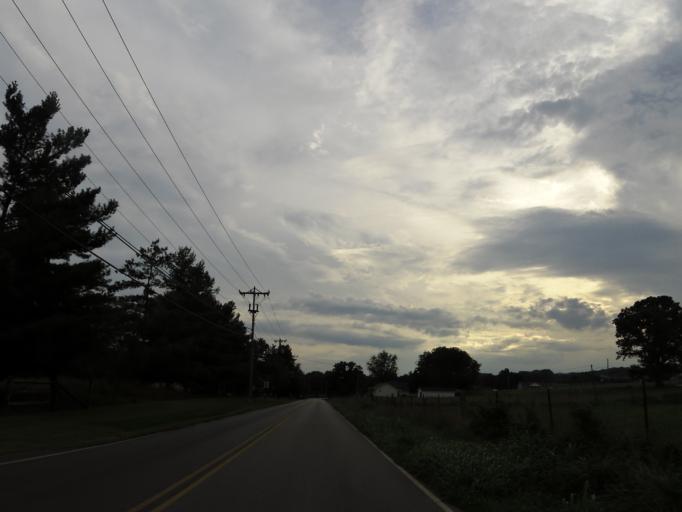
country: US
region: Tennessee
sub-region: Blount County
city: Maryville
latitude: 35.7170
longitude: -84.0583
